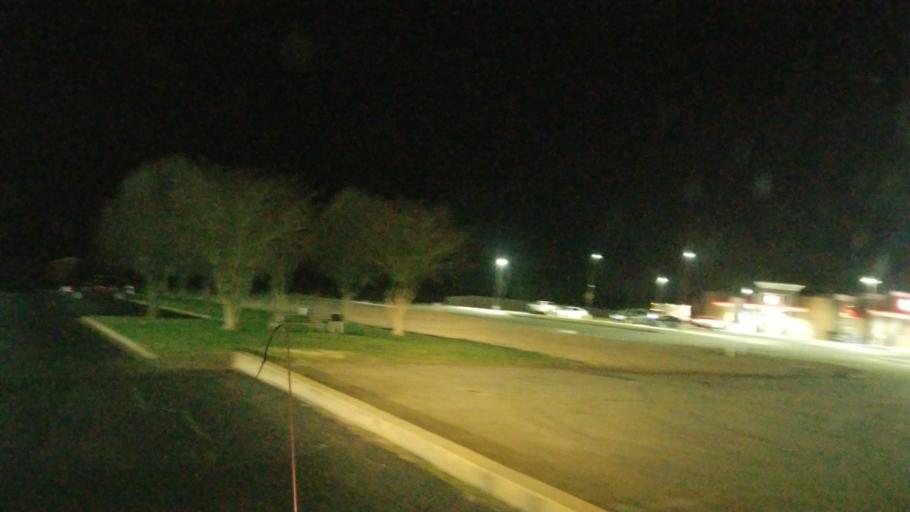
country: US
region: South Carolina
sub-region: York County
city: Catawba
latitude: 34.7442
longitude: -81.0318
